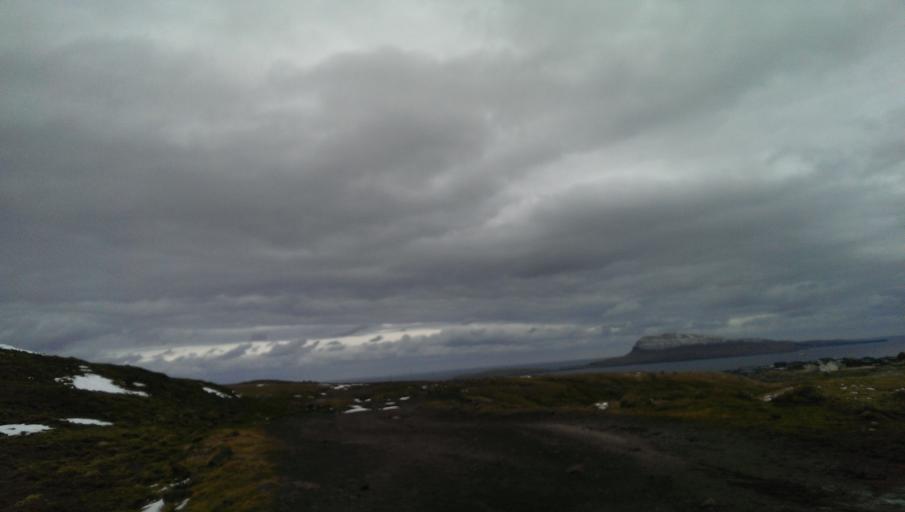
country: FO
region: Streymoy
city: Hoyvik
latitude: 62.0357
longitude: -6.8041
